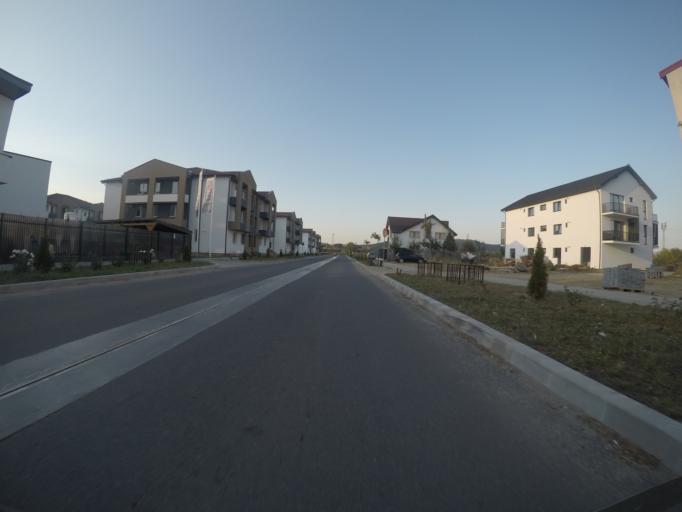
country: RO
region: Sibiu
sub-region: Comuna Selimbar
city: Selimbar
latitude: 45.7830
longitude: 24.1821
